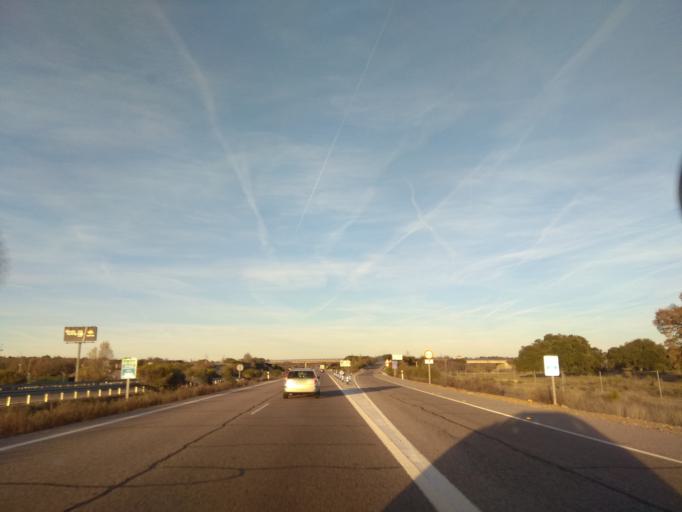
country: ES
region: Castille and Leon
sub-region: Provincia de Salamanca
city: Tenebron
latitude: 40.6638
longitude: -6.4364
